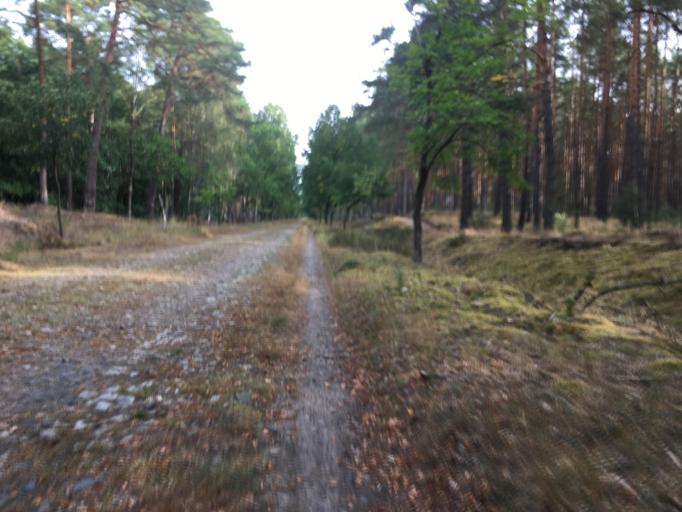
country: DE
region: Brandenburg
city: Marienwerder
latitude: 52.9317
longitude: 13.5191
